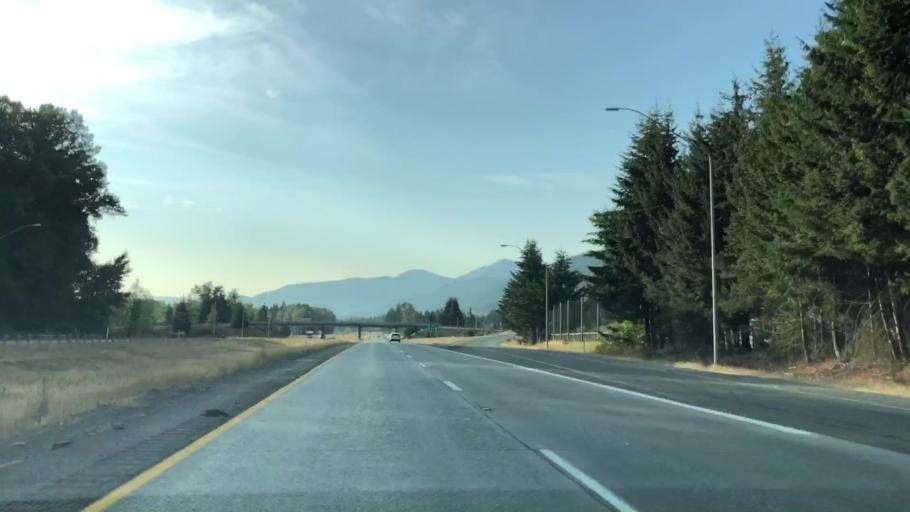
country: US
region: Washington
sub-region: Kittitas County
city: Cle Elum
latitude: 47.2410
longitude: -121.1740
